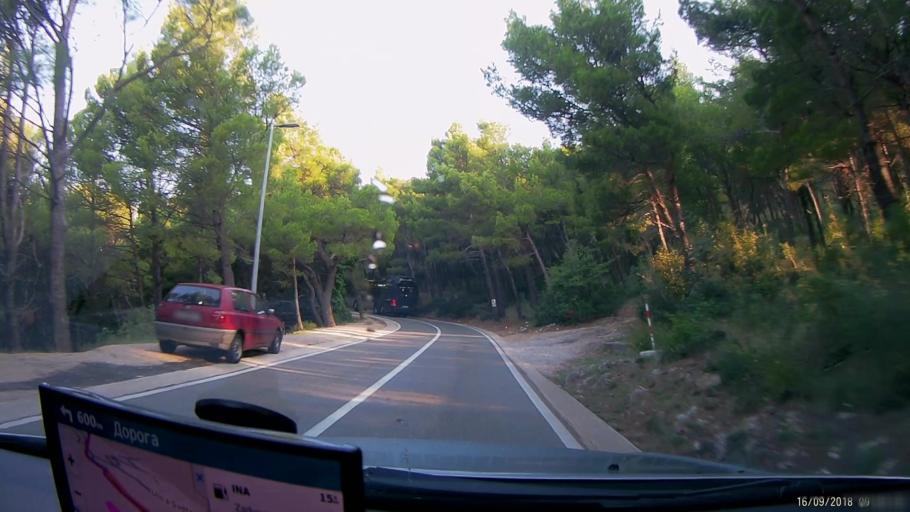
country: HR
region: Splitsko-Dalmatinska
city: Donja Brela
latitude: 43.3715
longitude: 16.9279
